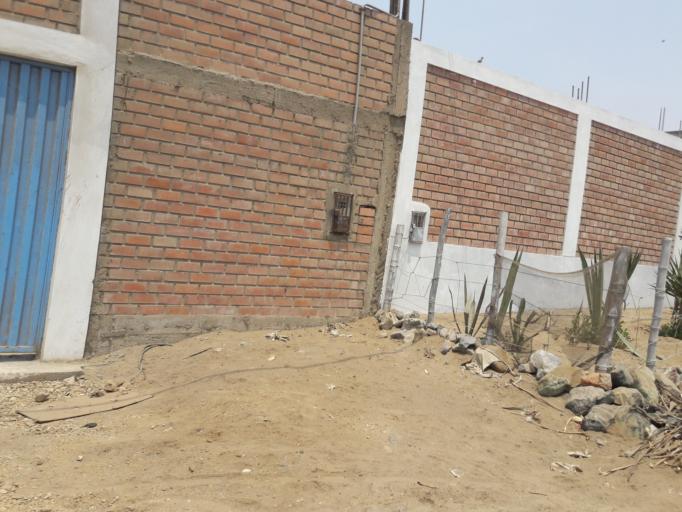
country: PE
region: Lima
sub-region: Lima
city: Santa Rosa
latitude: -11.7718
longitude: -77.1616
